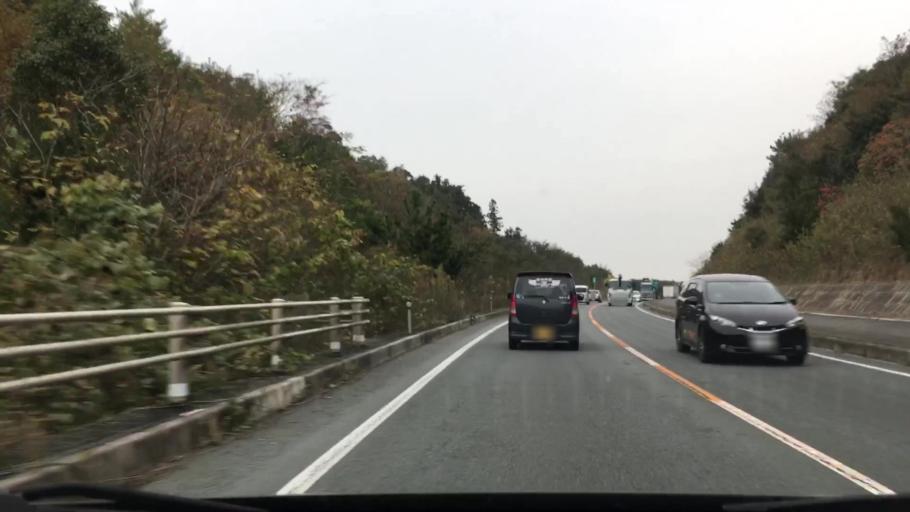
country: JP
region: Yamaguchi
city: Onoda
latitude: 34.0448
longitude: 131.1469
